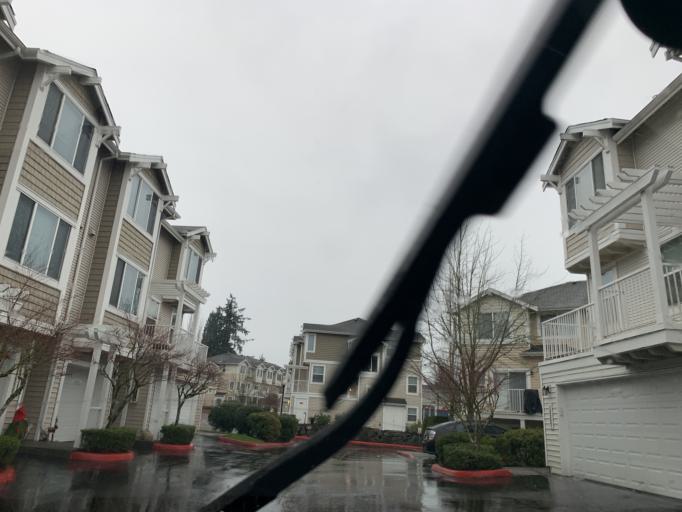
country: US
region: Washington
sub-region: King County
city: Kingsgate
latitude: 47.7470
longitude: -122.1828
